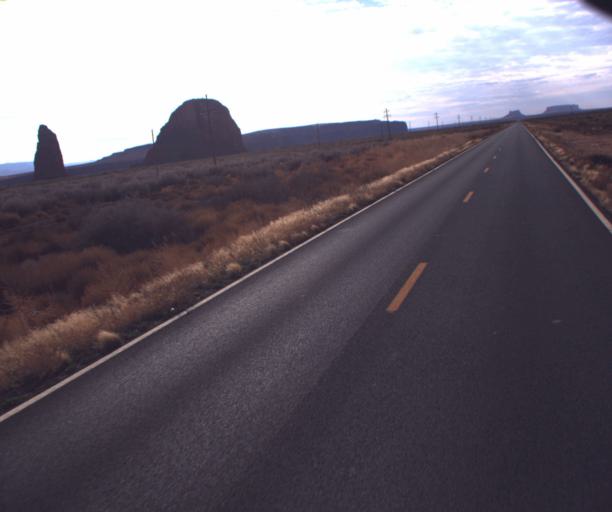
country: US
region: Arizona
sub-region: Apache County
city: Many Farms
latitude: 36.6734
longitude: -109.6002
